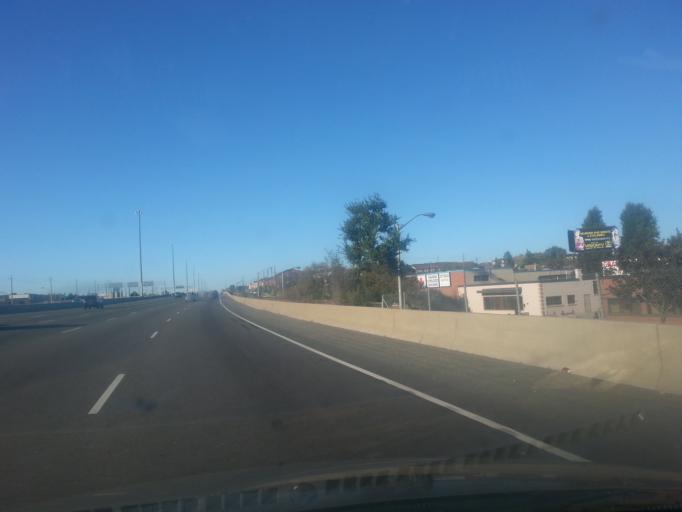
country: CA
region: Ontario
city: Etobicoke
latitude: 43.7228
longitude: -79.5229
